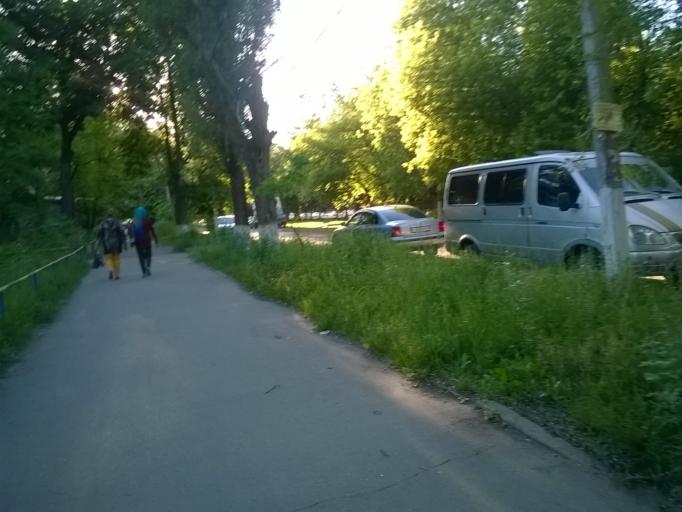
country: RU
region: Kursk
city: Kursk
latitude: 51.6694
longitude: 36.1495
